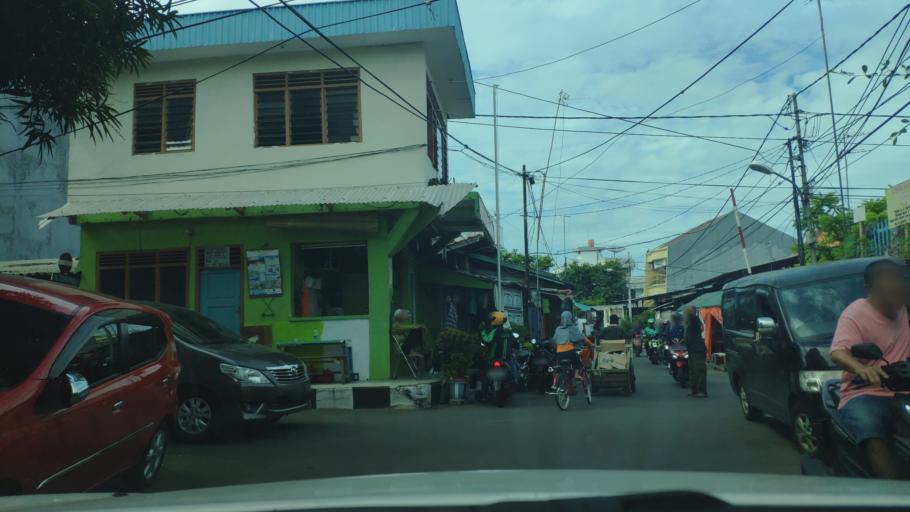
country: ID
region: Jakarta Raya
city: Jakarta
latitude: -6.1412
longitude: 106.8190
